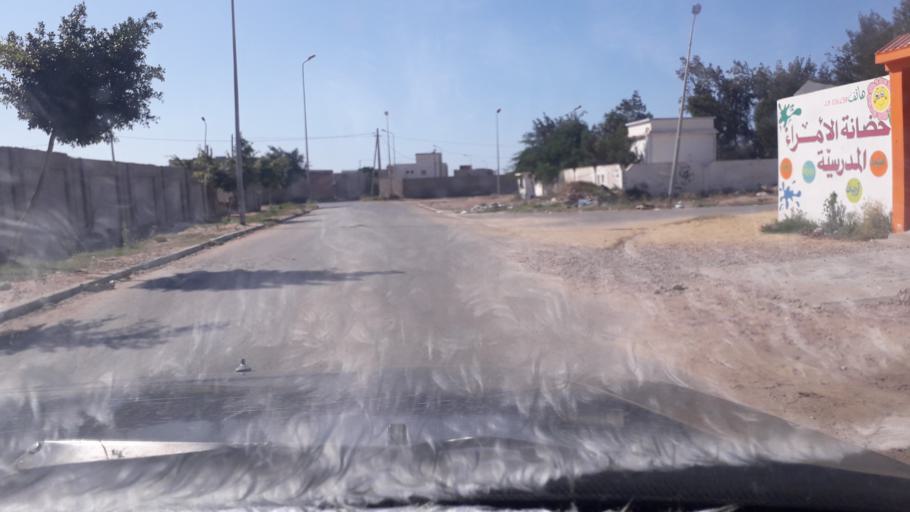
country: TN
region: Safaqis
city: Al Qarmadah
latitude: 34.8247
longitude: 10.7505
